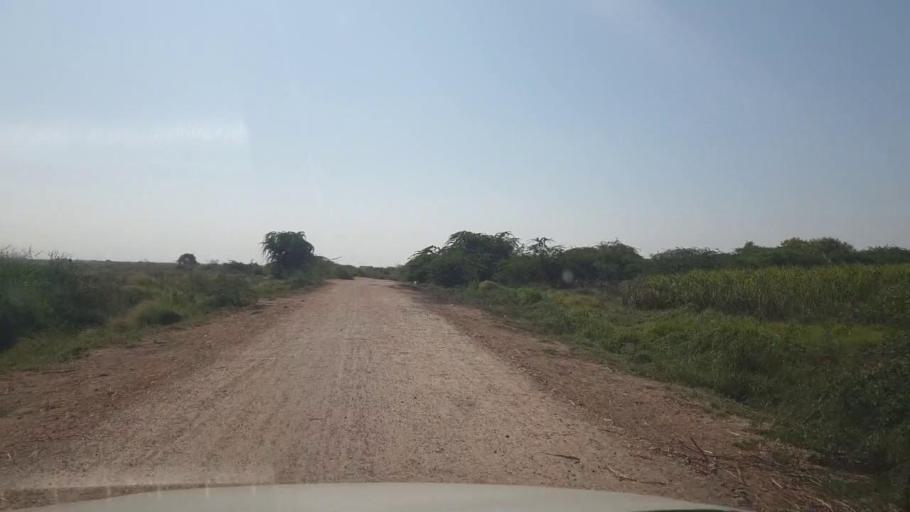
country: PK
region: Sindh
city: Mirpur Sakro
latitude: 24.4159
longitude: 67.7803
